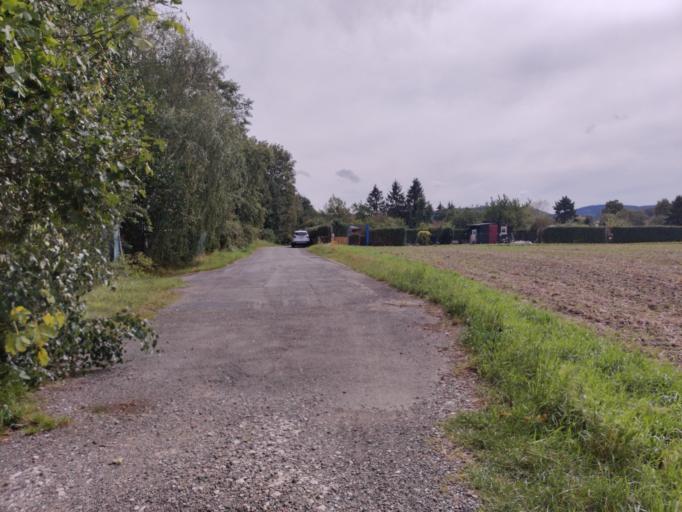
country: DE
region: Lower Saxony
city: Langelsheim
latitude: 51.9400
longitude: 10.3436
